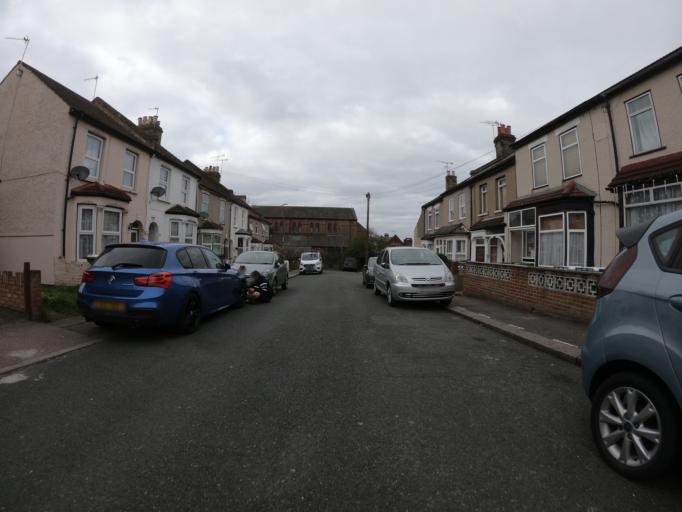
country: GB
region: England
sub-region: Greater London
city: Belvedere
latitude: 51.4904
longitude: 0.1455
